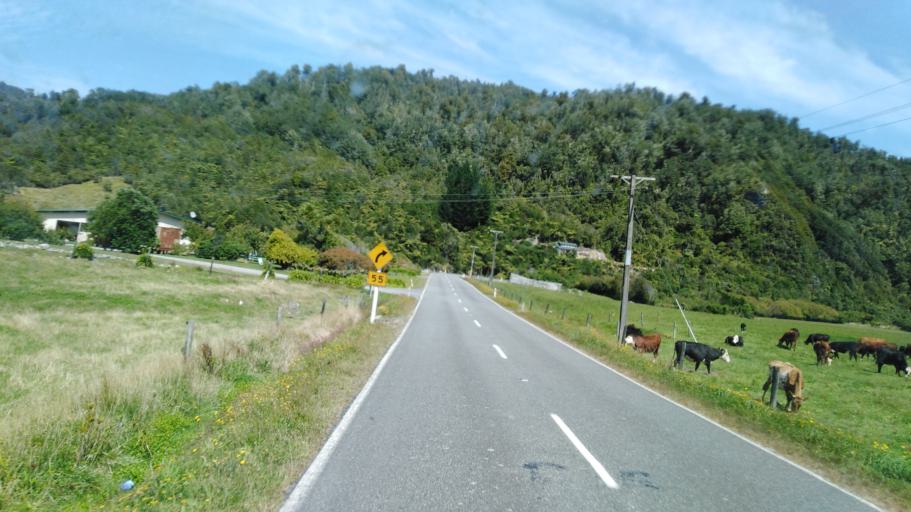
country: NZ
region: West Coast
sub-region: Buller District
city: Westport
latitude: -41.5328
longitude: 171.9619
